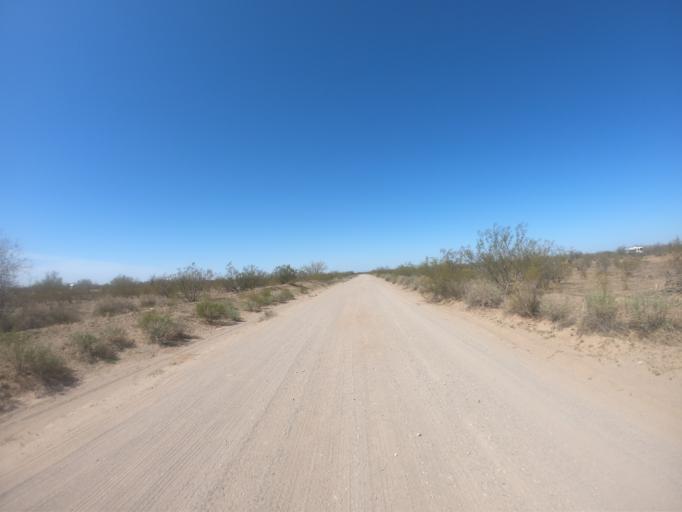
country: US
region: Arizona
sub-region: Pinal County
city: Gold Camp
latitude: 33.2393
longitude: -111.3374
